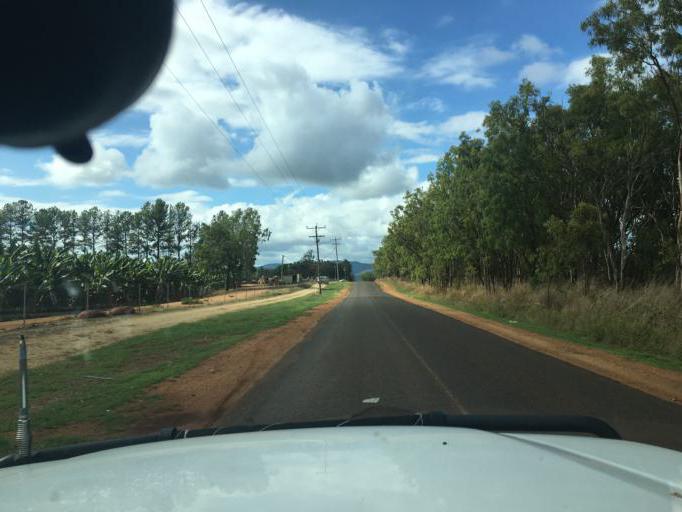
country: AU
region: Queensland
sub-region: Tablelands
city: Mareeba
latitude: -17.1004
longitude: 145.4117
